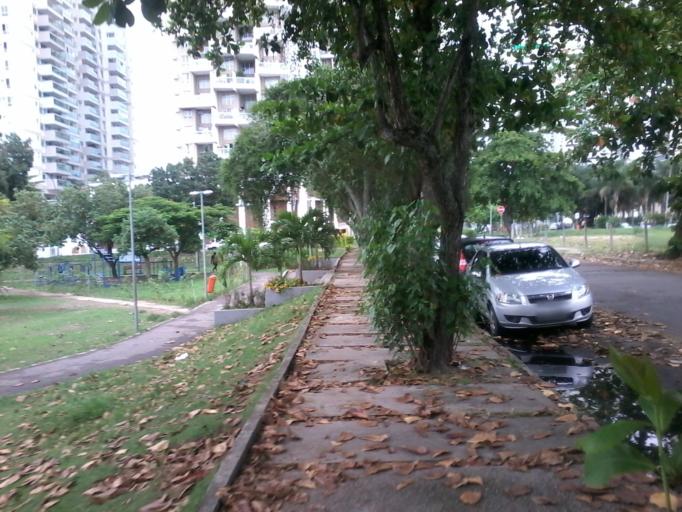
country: BR
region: Rio de Janeiro
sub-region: Nilopolis
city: Nilopolis
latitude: -23.0236
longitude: -43.4871
